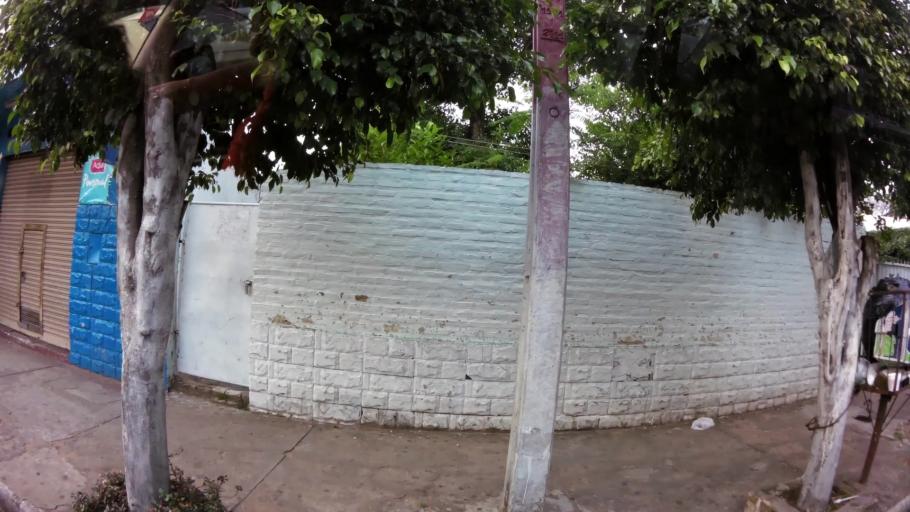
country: PY
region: Central
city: Lambare
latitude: -25.3439
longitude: -57.6156
